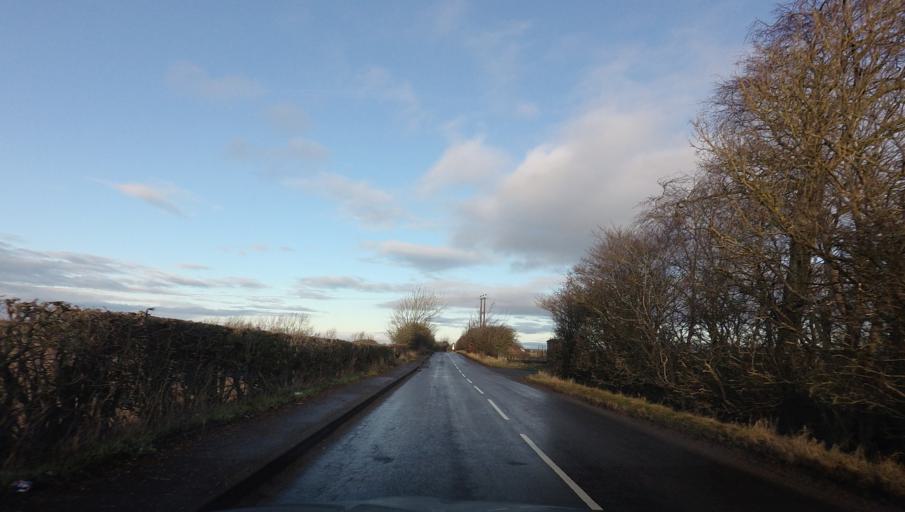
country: GB
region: Scotland
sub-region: West Lothian
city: East Calder
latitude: 55.8937
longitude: -3.4417
